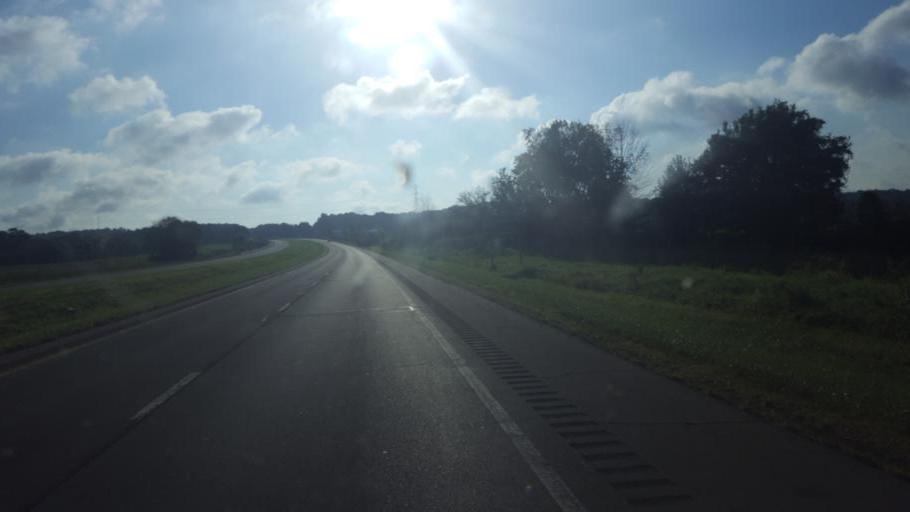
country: US
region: Ohio
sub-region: Wayne County
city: Shreve
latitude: 40.7843
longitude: -82.1018
